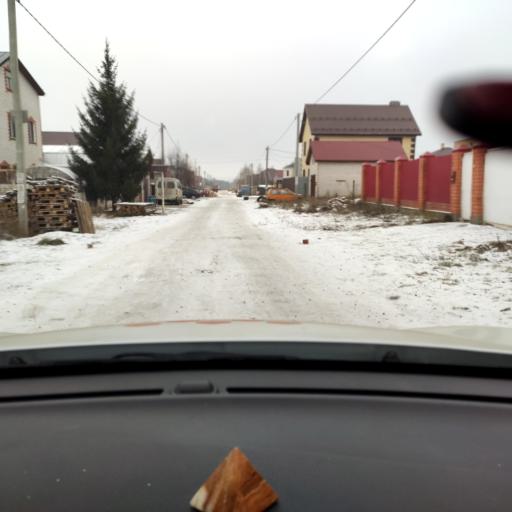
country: RU
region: Tatarstan
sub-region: Gorod Kazan'
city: Kazan
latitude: 55.7800
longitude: 49.2606
